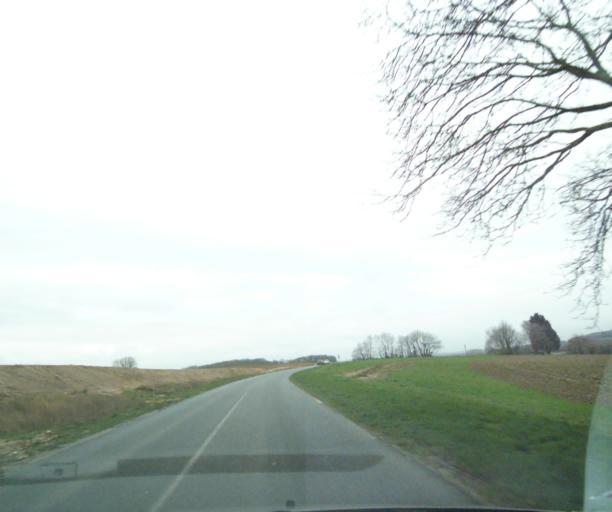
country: FR
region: Picardie
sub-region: Departement de l'Oise
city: Noyon
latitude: 49.5736
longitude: 2.9713
